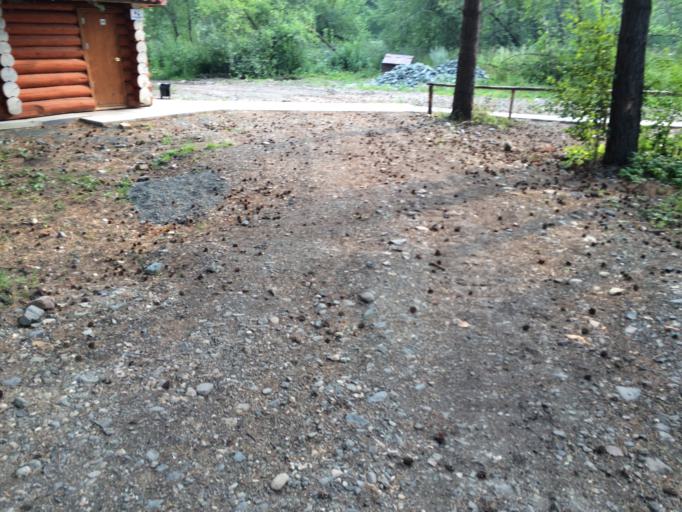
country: RU
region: Bashkortostan
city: Abzakovo
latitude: 53.7953
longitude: 58.6297
